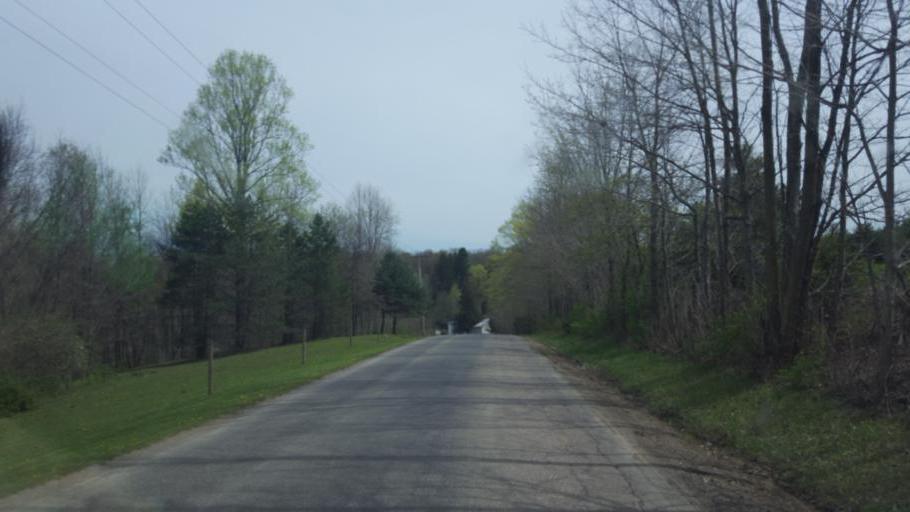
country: US
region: Ohio
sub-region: Richland County
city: Lexington
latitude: 40.5705
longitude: -82.6230
